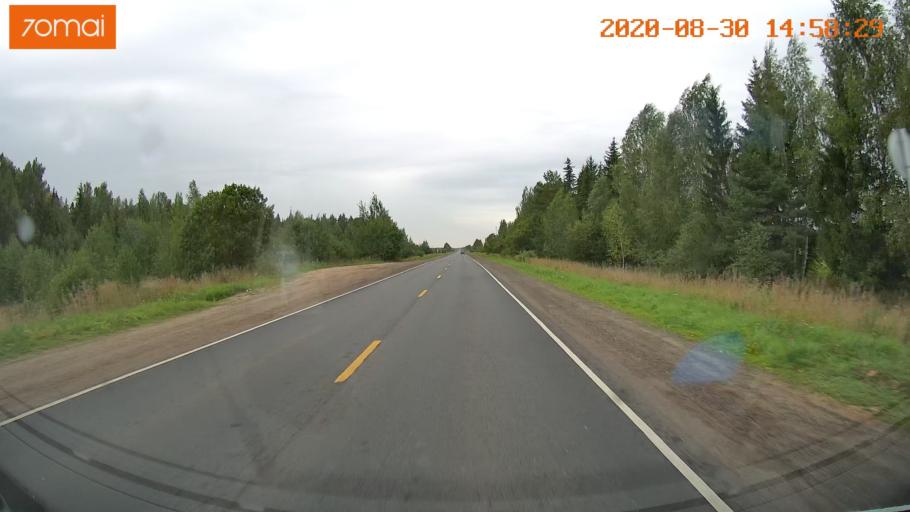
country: RU
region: Ivanovo
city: Navoloki
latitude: 57.3516
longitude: 41.9888
